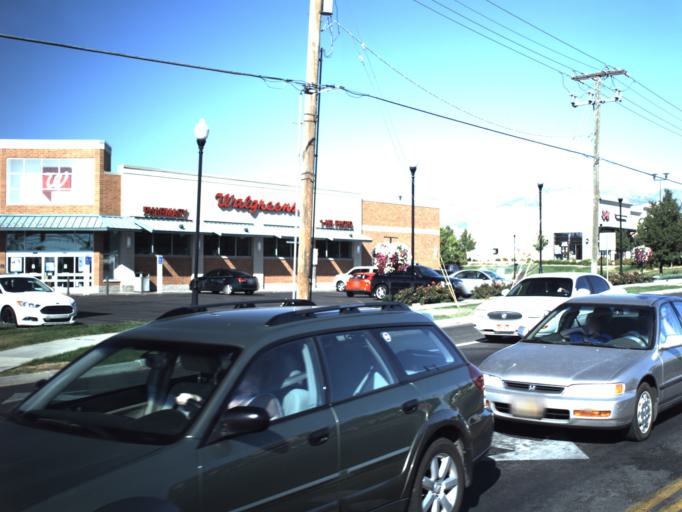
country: US
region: Utah
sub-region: Davis County
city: Clinton
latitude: 41.1398
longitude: -112.0643
